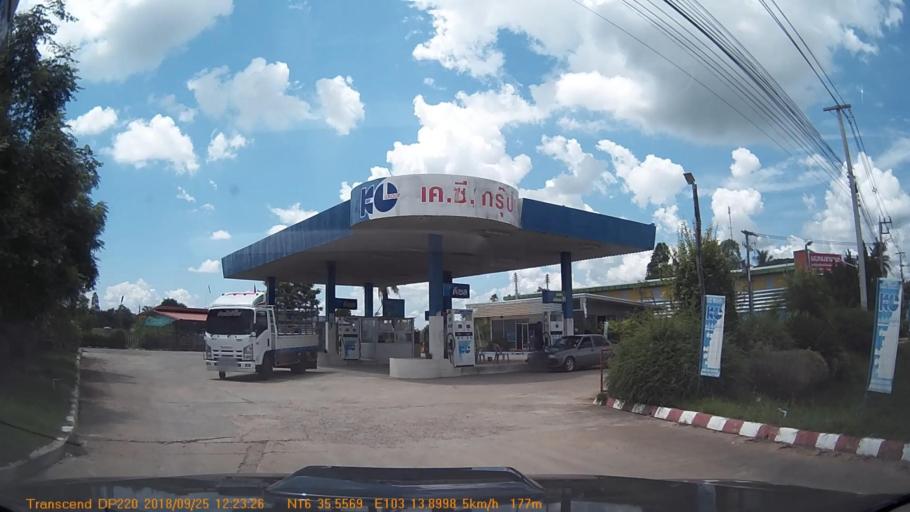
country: TH
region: Kalasin
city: Huai Mek
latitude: 16.5924
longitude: 103.2319
